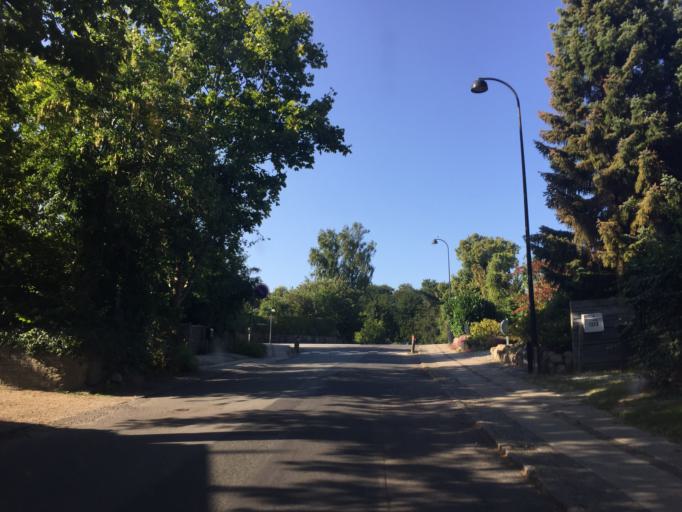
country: DK
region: Capital Region
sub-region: Lyngby-Tarbaek Kommune
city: Kongens Lyngby
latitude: 55.7657
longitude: 12.5359
